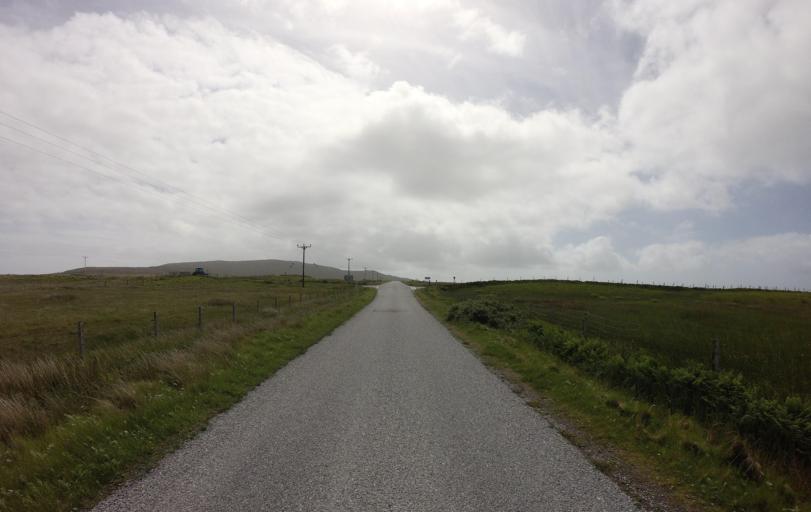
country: GB
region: Scotland
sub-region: Eilean Siar
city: Isle of South Uist
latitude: 57.1382
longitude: -7.3668
